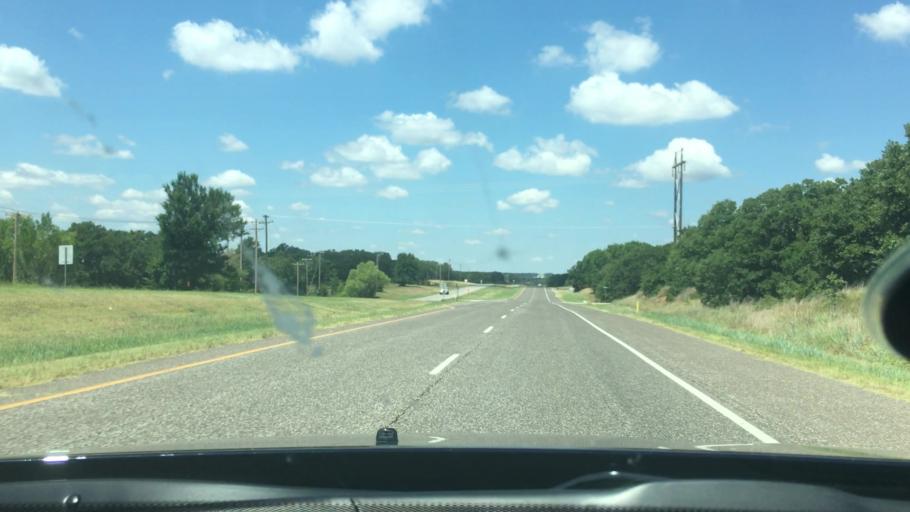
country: US
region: Oklahoma
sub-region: Carter County
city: Lone Grove
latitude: 34.1730
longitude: -97.3331
